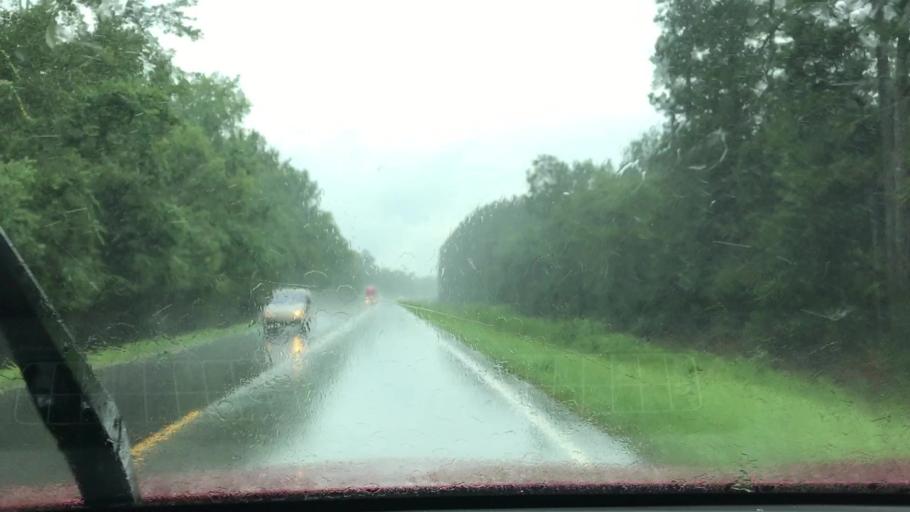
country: US
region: South Carolina
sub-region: Horry County
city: Socastee
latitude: 33.6810
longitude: -79.1268
